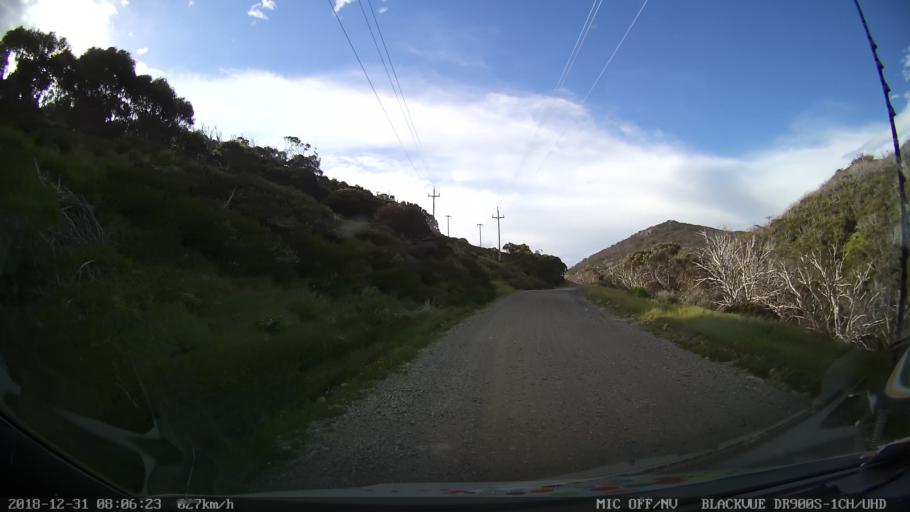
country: AU
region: New South Wales
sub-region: Snowy River
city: Jindabyne
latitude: -36.3744
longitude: 148.4081
